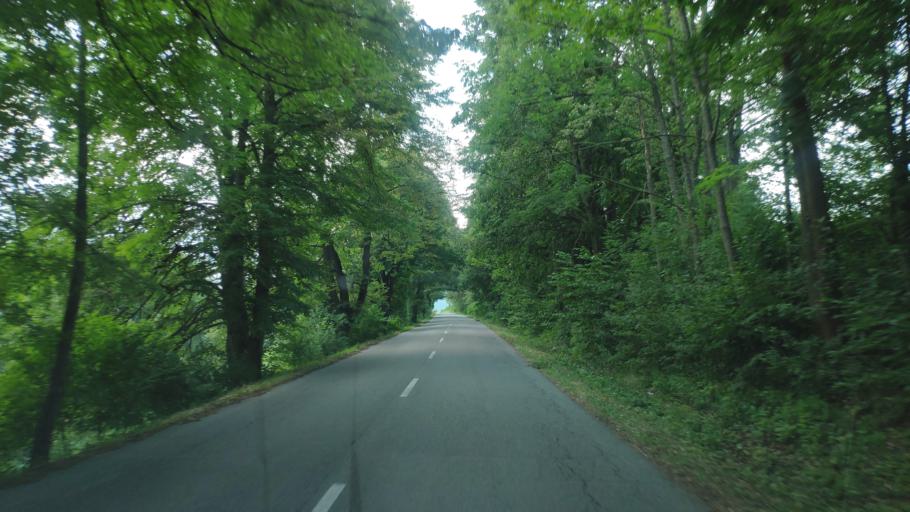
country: SK
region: Kosicky
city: Medzev
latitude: 48.6920
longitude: 20.9739
